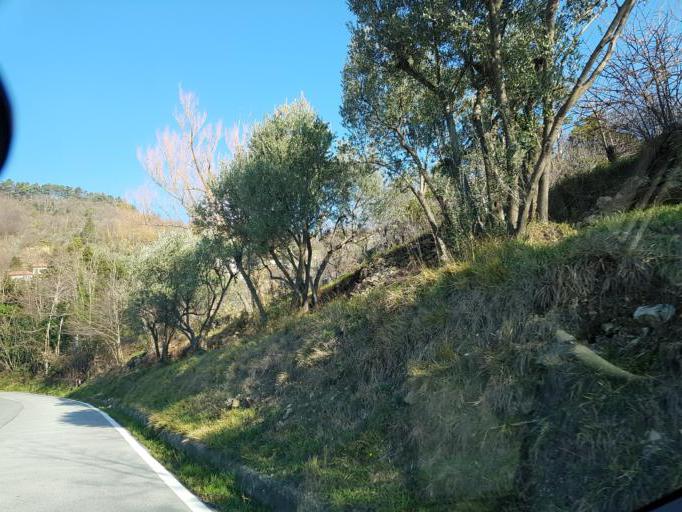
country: IT
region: Liguria
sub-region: Provincia di Genova
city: Piccarello
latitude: 44.4585
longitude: 8.9525
